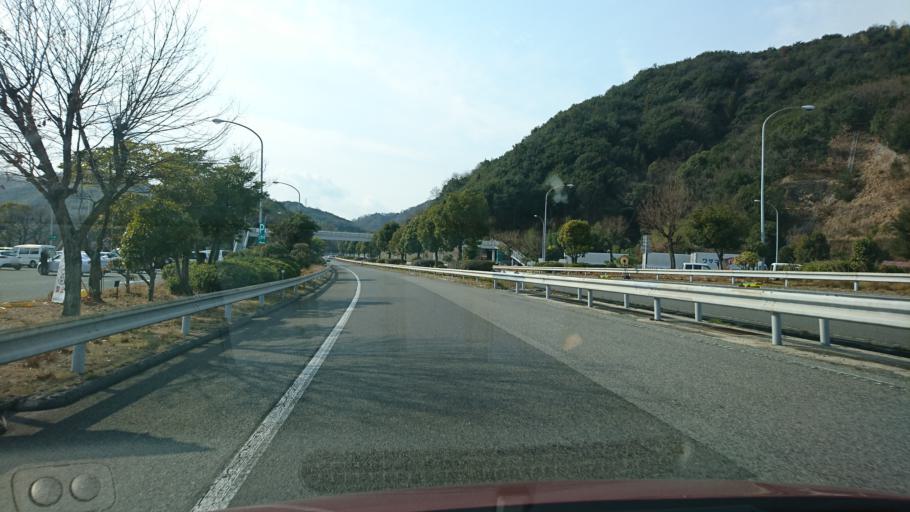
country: JP
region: Hiroshima
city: Onomichi
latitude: 34.3528
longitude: 133.1705
